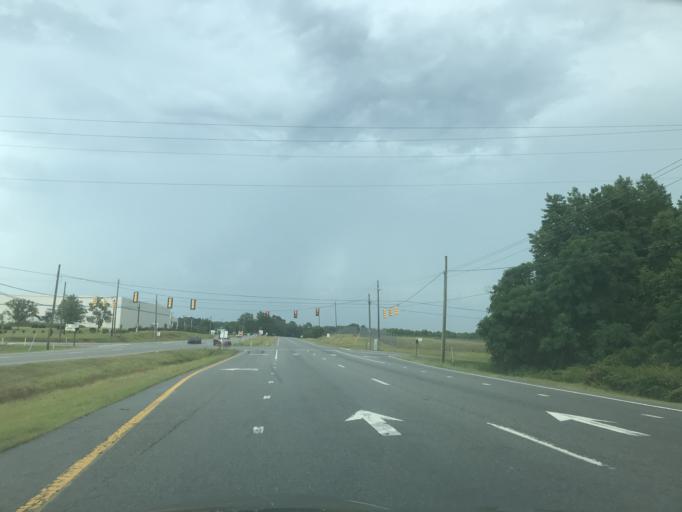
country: US
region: North Carolina
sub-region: Johnston County
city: Wilsons Mills
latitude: 35.5558
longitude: -78.3872
